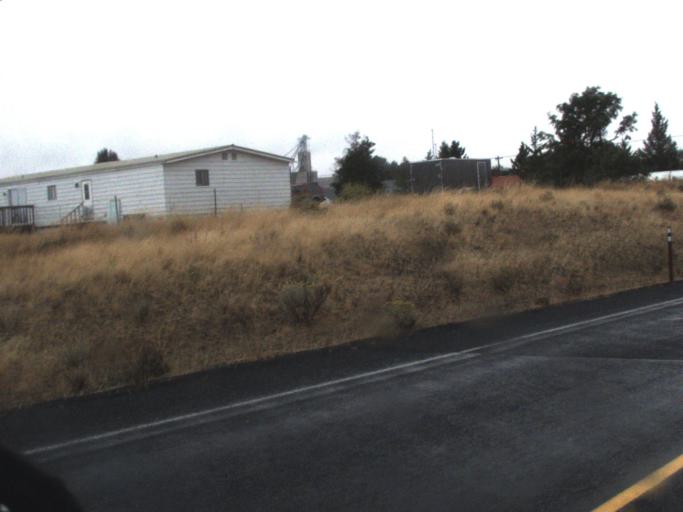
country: US
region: Washington
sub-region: Lincoln County
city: Davenport
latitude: 47.2969
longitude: -117.9738
